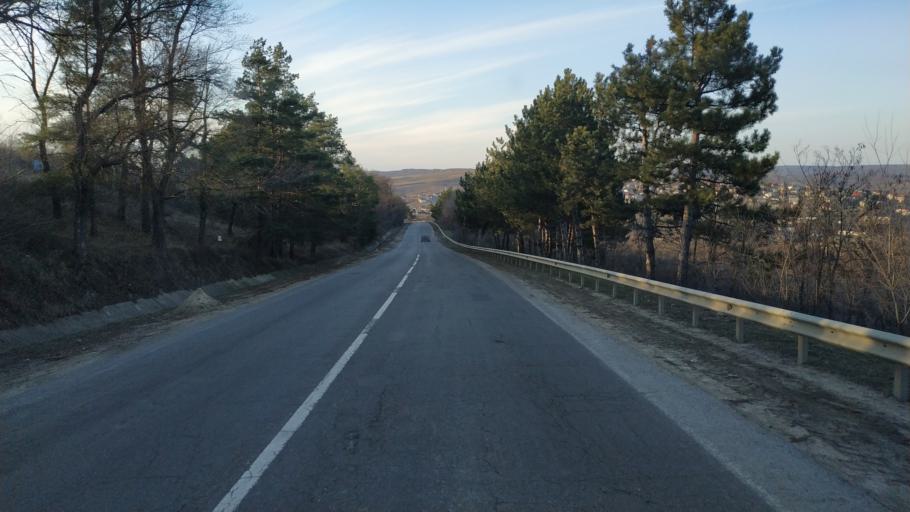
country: MD
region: Hincesti
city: Hincesti
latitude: 46.8280
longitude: 28.5747
